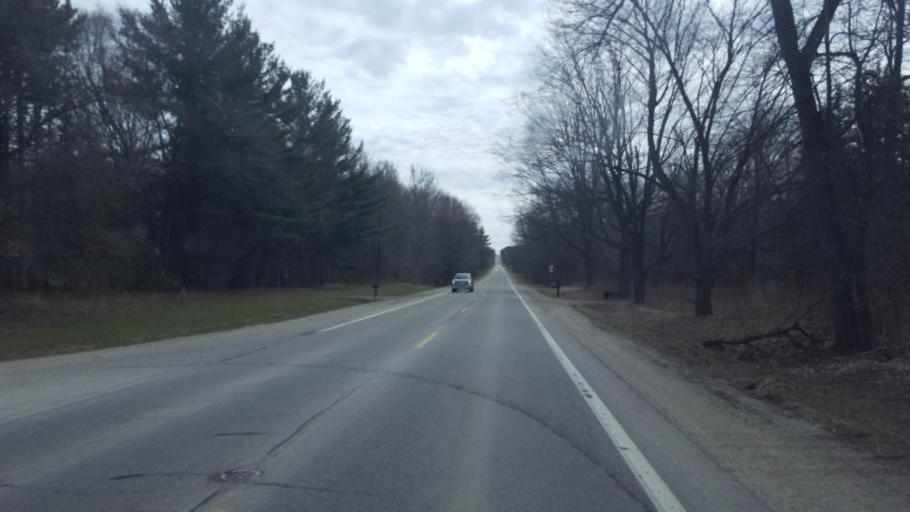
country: US
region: Michigan
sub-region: Isabella County
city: Lake Isabella
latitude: 43.6973
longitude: -85.1467
